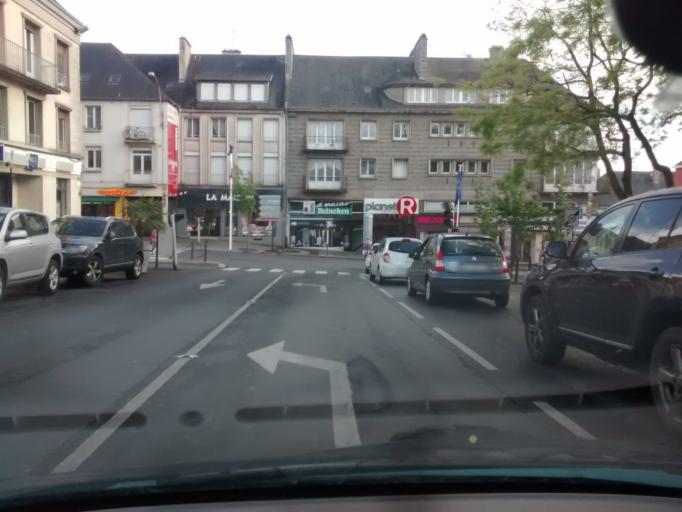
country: FR
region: Lower Normandy
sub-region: Departement de la Manche
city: Saint-Lo
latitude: 49.1153
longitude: -1.0900
